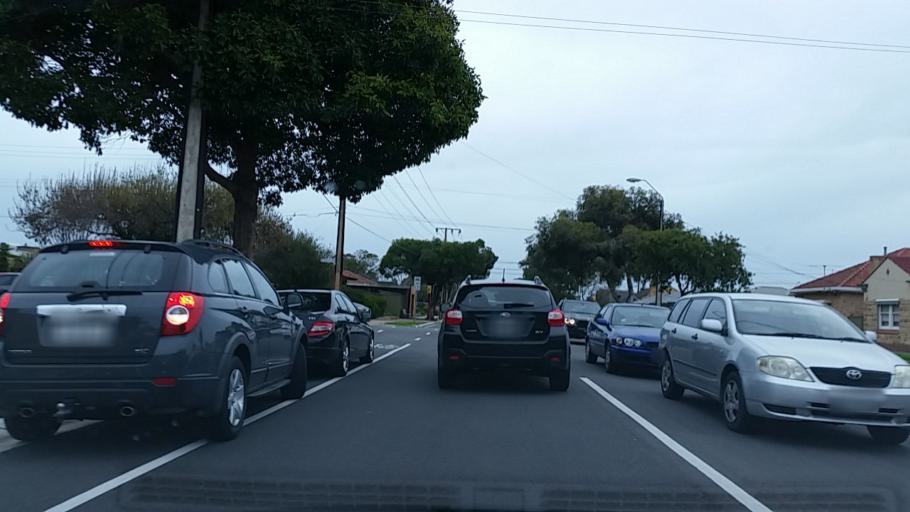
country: AU
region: South Australia
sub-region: Charles Sturt
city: Allenby Gardens
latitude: -34.9117
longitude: 138.5456
